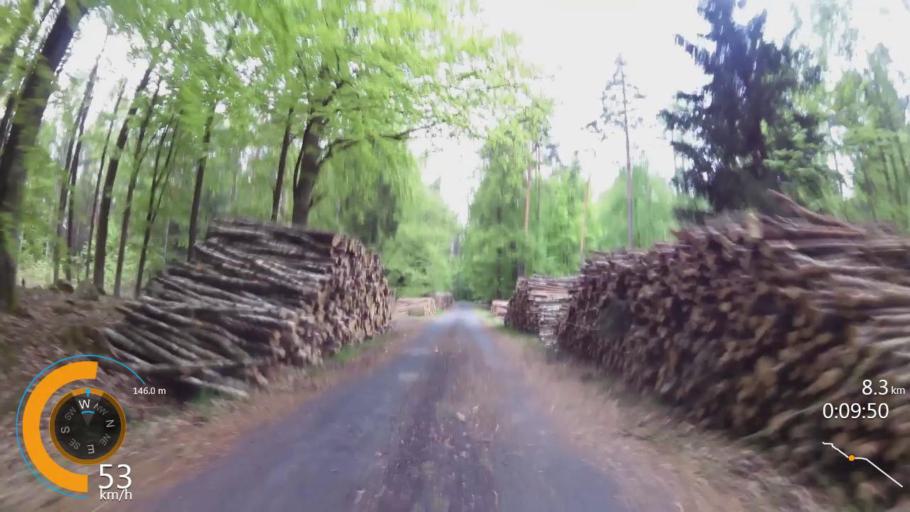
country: PL
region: West Pomeranian Voivodeship
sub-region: Powiat drawski
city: Wierzchowo
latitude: 53.5038
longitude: 16.1302
